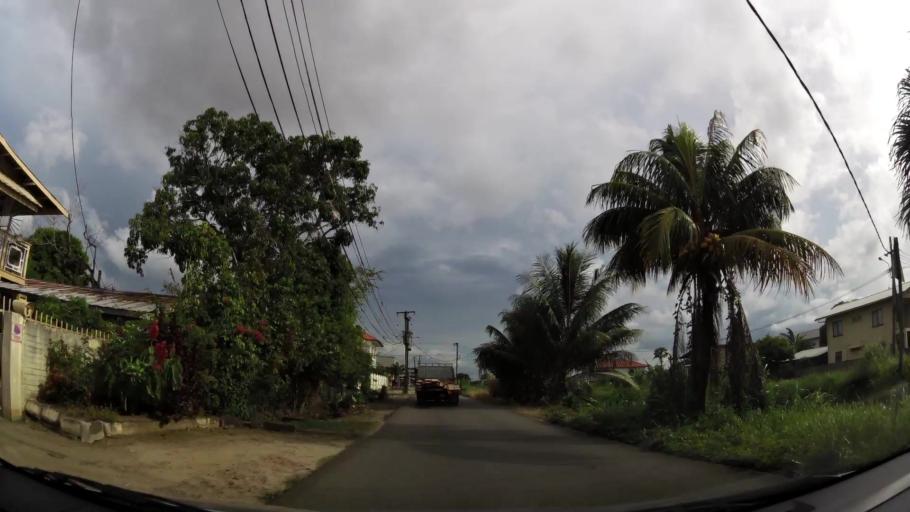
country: SR
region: Paramaribo
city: Paramaribo
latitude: 5.8568
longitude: -55.1833
